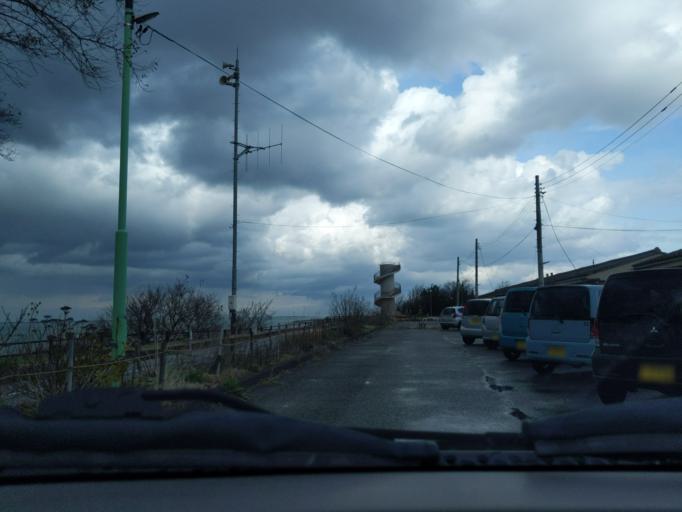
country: JP
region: Niigata
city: Niigata-shi
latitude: 37.9331
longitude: 139.0426
